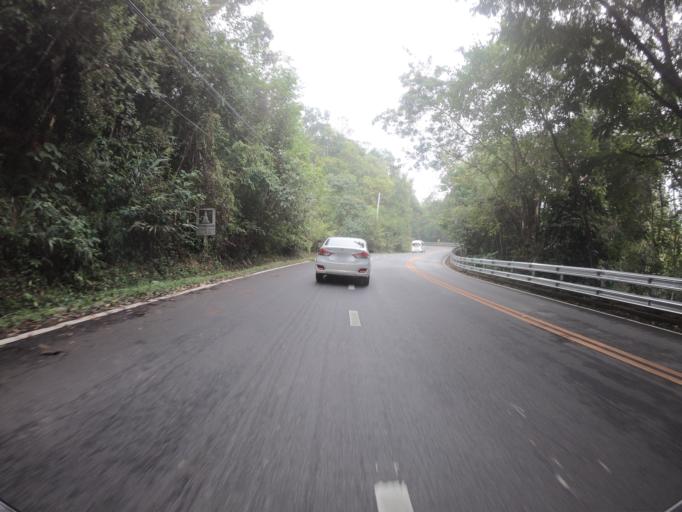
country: TH
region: Chiang Mai
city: Chiang Mai
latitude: 18.7989
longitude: 98.9220
